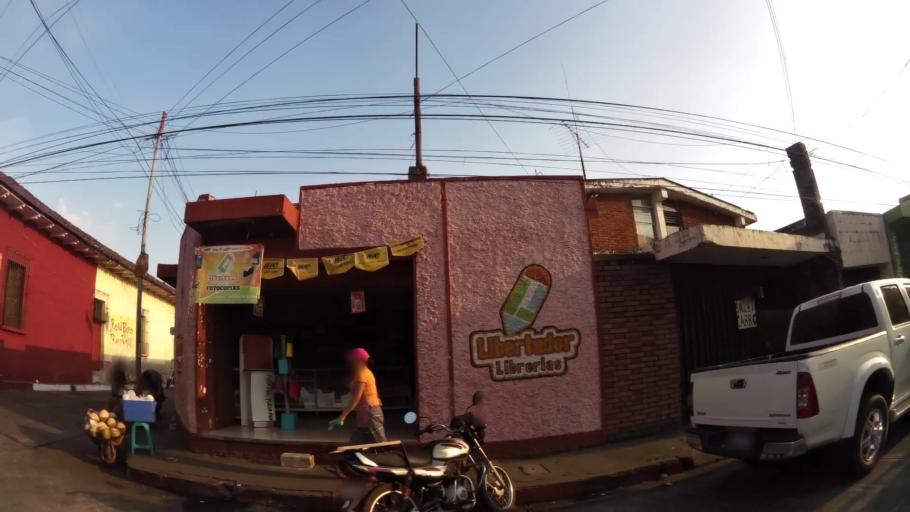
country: GT
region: Retalhuleu
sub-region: Municipio de Retalhuleu
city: Retalhuleu
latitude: 14.5360
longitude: -91.6796
